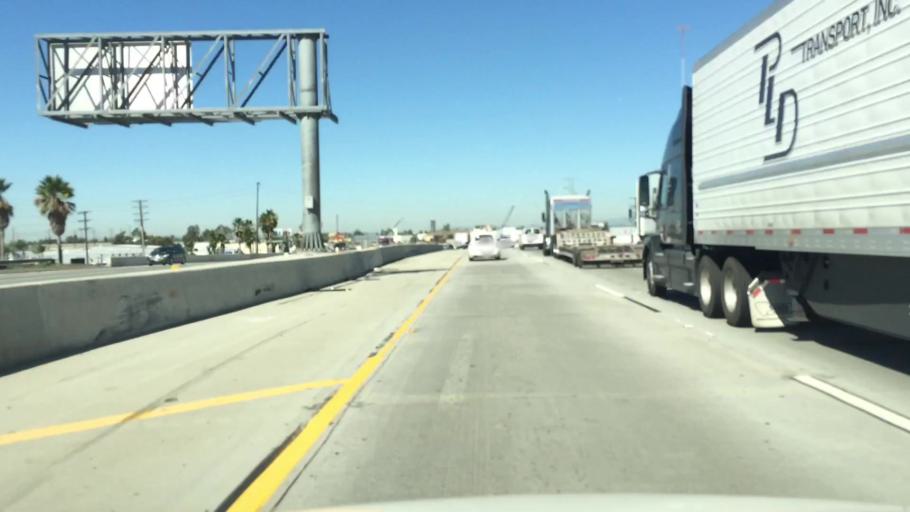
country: US
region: California
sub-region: Orange County
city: Buena Park
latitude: 33.8729
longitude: -118.0092
